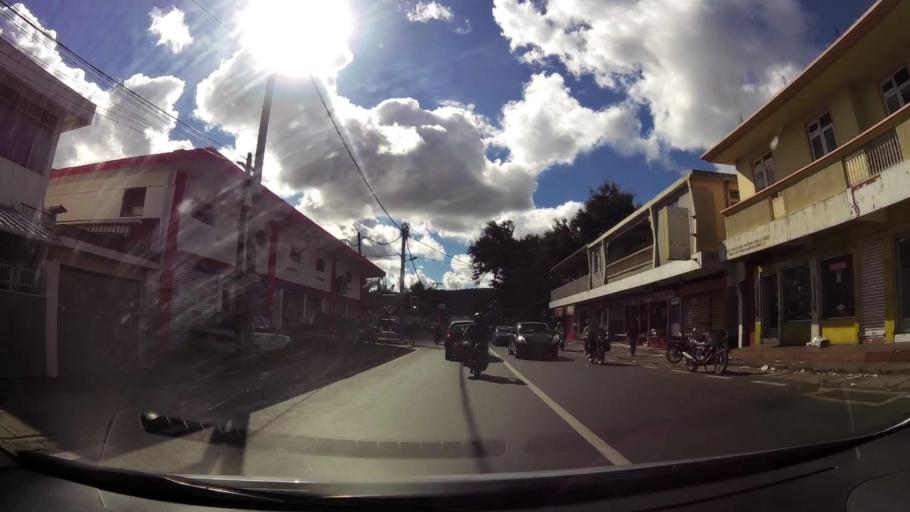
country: MU
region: Pamplemousses
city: Le Hochet
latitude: -20.1483
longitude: 57.5195
